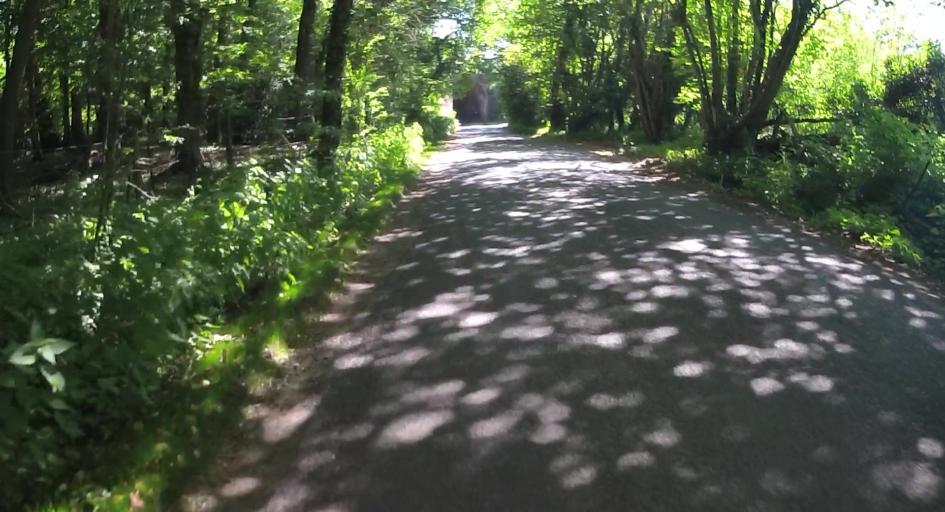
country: GB
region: England
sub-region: Hampshire
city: Hook
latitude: 51.2775
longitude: -0.9948
